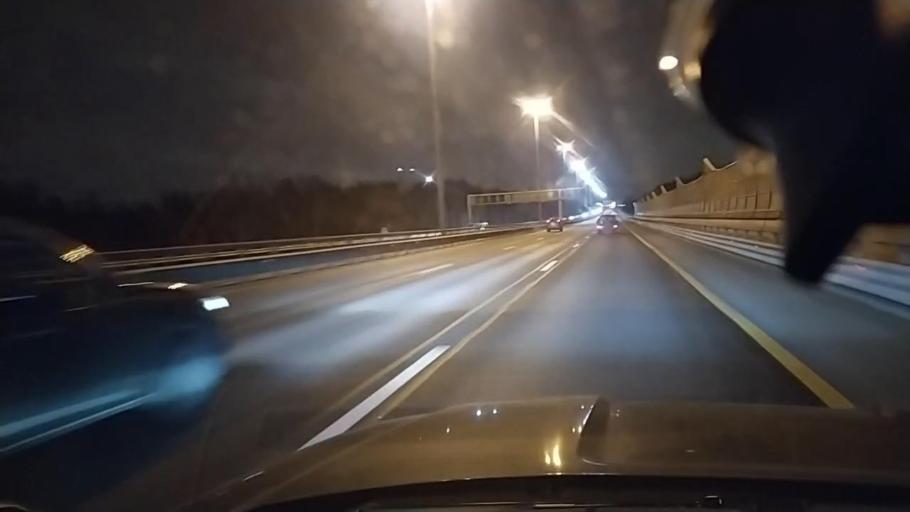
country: RU
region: Leningrad
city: Untolovo
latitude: 60.0345
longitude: 30.1869
